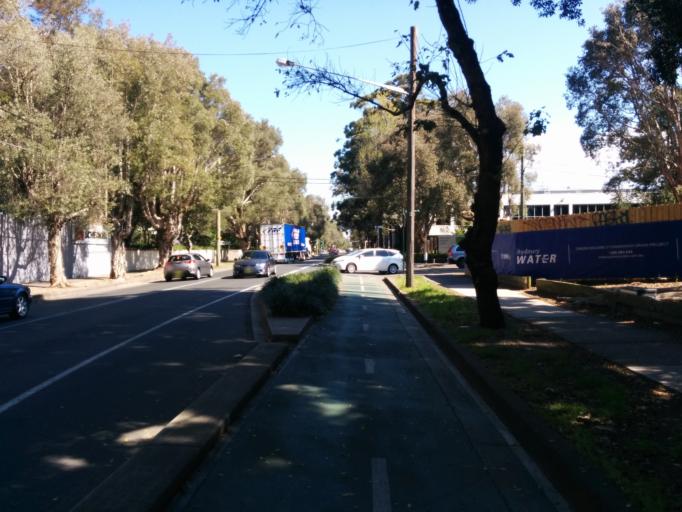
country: AU
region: New South Wales
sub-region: City of Sydney
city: Alexandria
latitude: -33.9087
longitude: 151.1970
